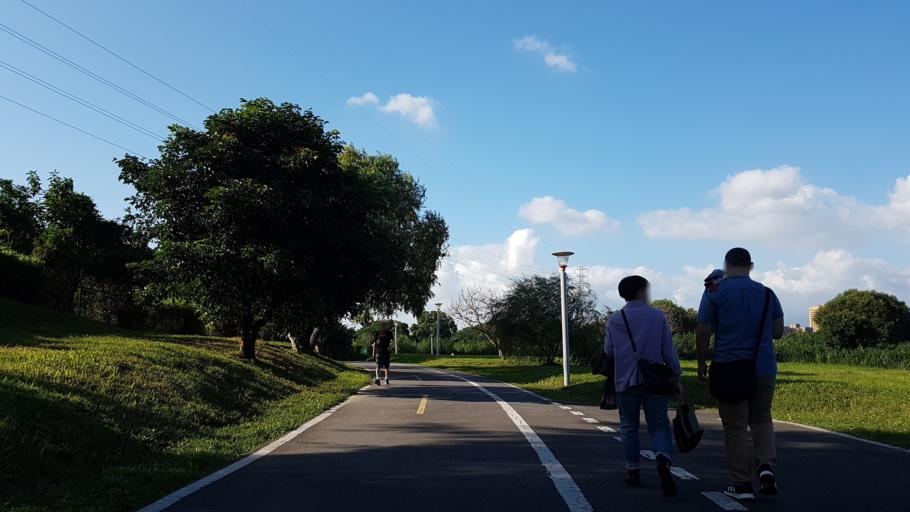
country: TW
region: Taipei
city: Taipei
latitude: 25.0026
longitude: 121.5312
